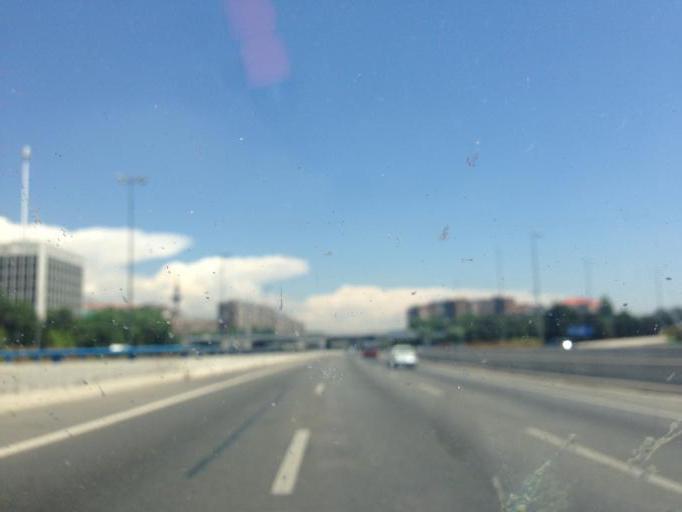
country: ES
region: Madrid
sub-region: Provincia de Madrid
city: Puente de Vallecas
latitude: 40.4037
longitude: -3.6664
